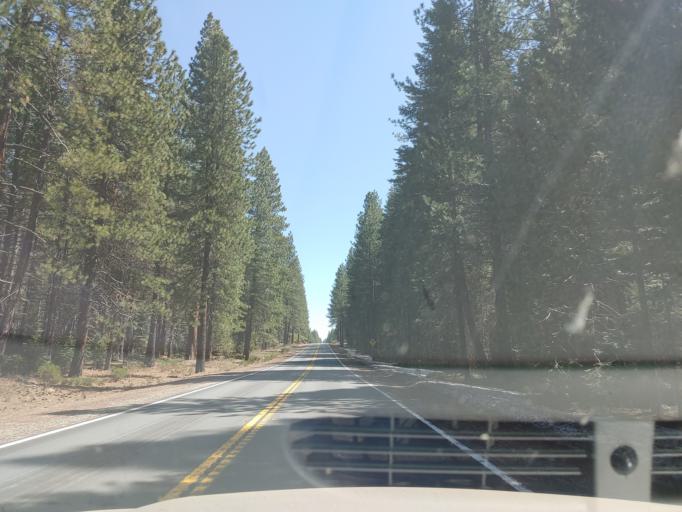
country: US
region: California
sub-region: Siskiyou County
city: McCloud
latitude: 41.2676
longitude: -121.9112
